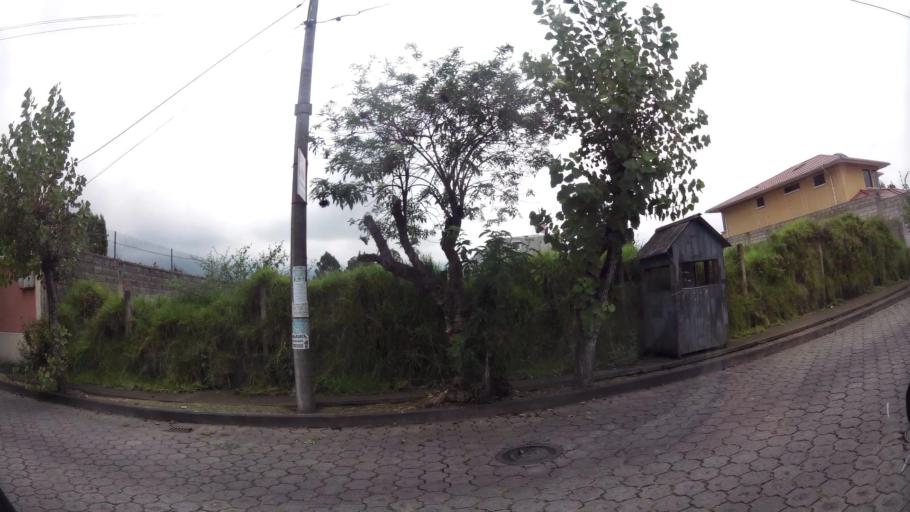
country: EC
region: Pichincha
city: Sangolqui
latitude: -0.3115
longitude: -78.4640
